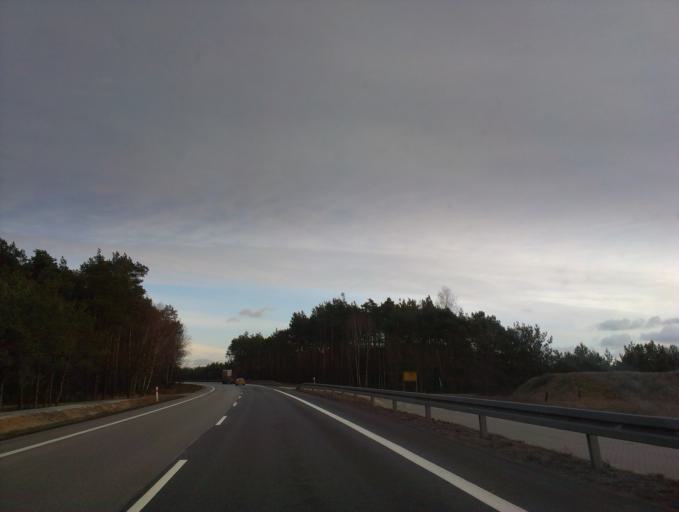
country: PL
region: Kujawsko-Pomorskie
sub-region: Powiat lipnowski
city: Skepe
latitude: 52.8754
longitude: 19.3506
